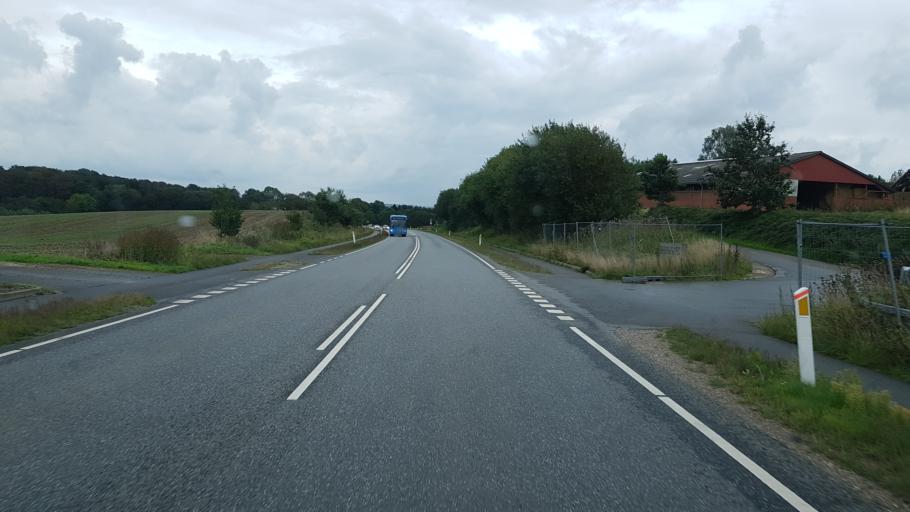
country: DK
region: Central Jutland
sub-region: Horsens Kommune
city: Braedstrup
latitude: 55.9093
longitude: 9.7210
